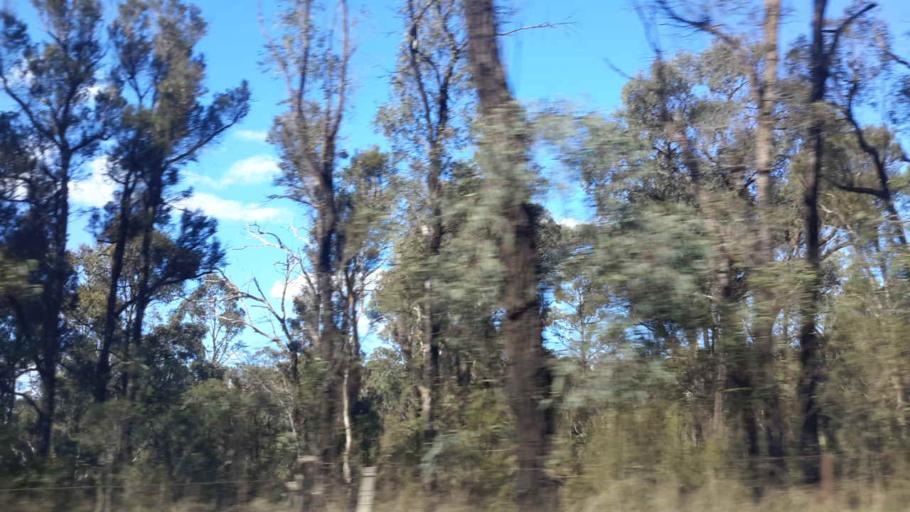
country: AU
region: New South Wales
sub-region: Hawkesbury
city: South Windsor
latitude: -33.6434
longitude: 150.7879
